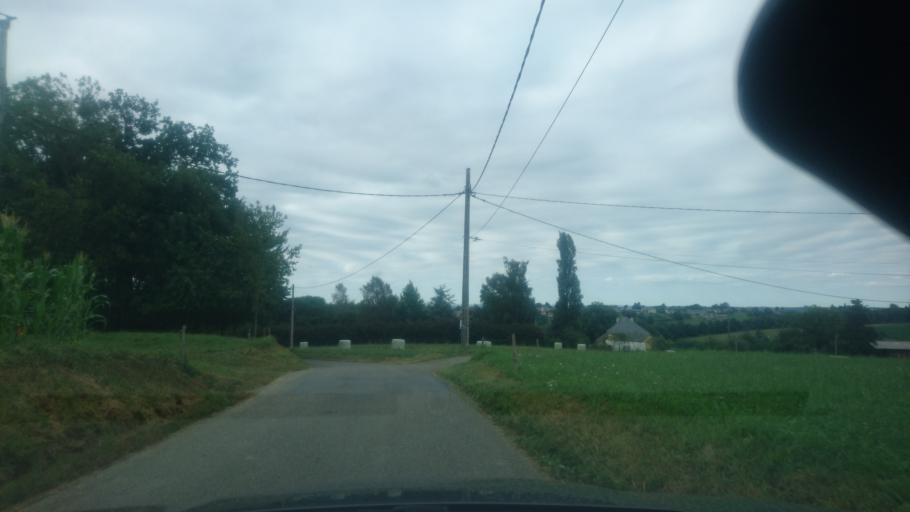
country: FR
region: Midi-Pyrenees
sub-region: Departement des Hautes-Pyrenees
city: Horgues
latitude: 43.1286
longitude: 0.0623
